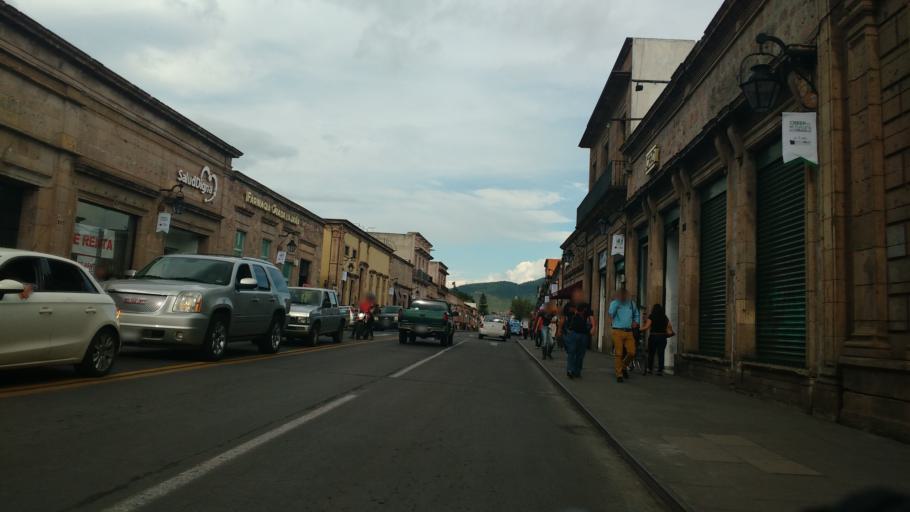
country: MX
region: Michoacan
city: Morelia
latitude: 19.7028
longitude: -101.1859
